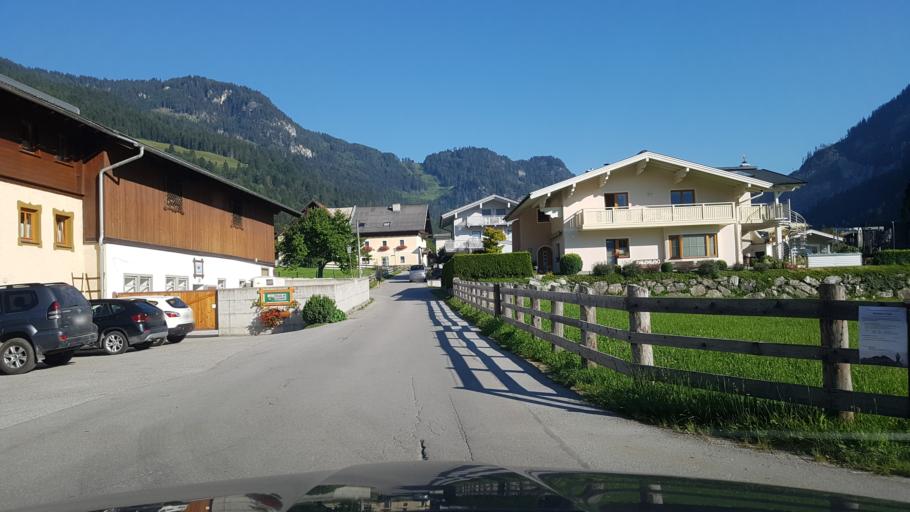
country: AT
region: Salzburg
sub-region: Politischer Bezirk Sankt Johann im Pongau
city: Dorfgastein
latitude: 47.2561
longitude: 13.0847
